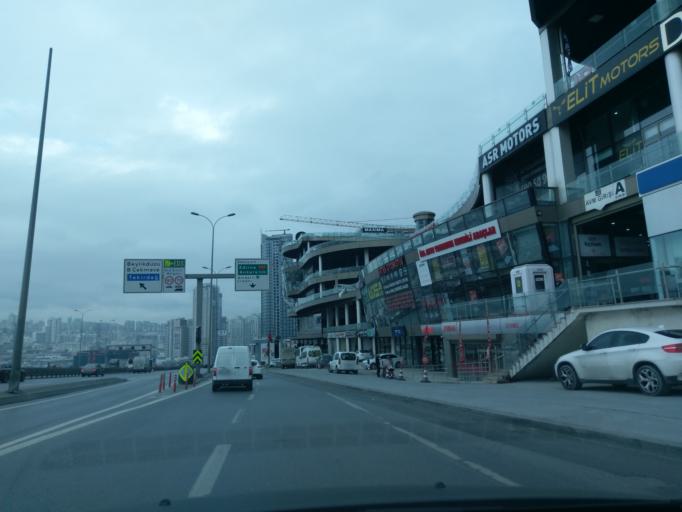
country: TR
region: Istanbul
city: Yakuplu
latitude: 41.0013
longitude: 28.6894
